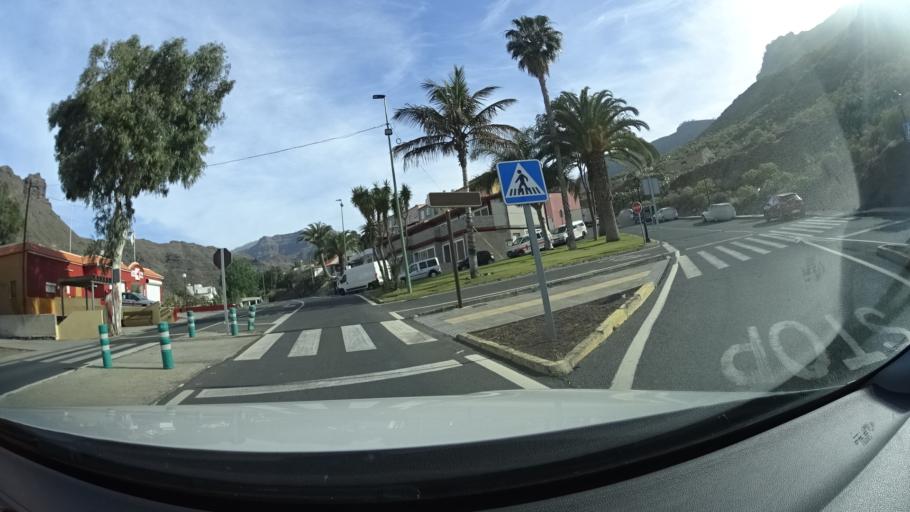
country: ES
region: Canary Islands
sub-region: Provincia de Las Palmas
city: Mogan
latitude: 27.8788
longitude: -15.7262
